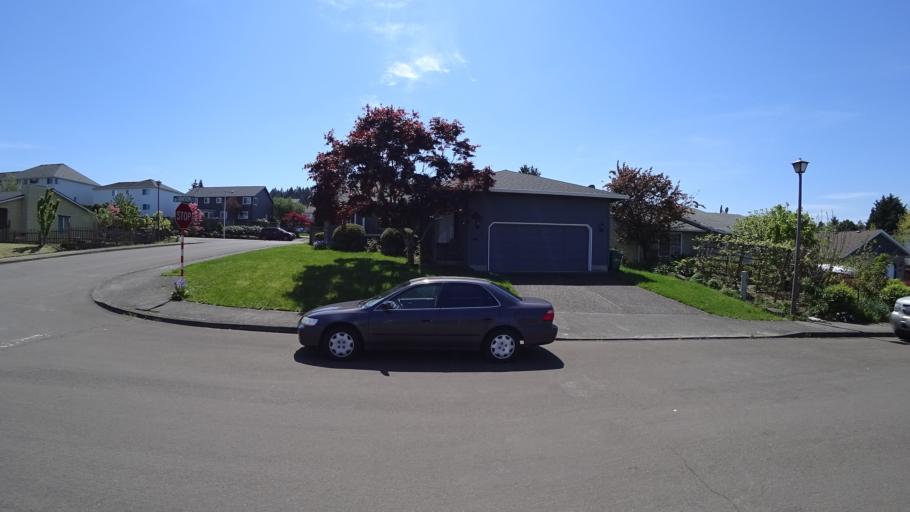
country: US
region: Oregon
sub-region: Washington County
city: King City
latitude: 45.4322
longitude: -122.8191
